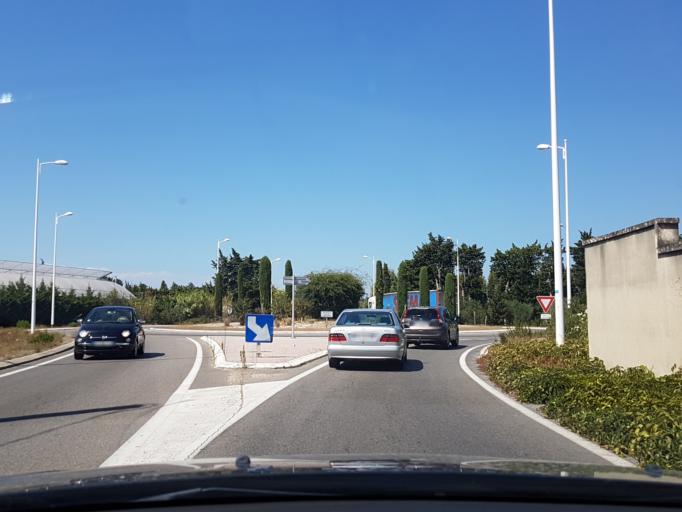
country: FR
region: Provence-Alpes-Cote d'Azur
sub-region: Departement des Bouches-du-Rhone
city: Rognonas
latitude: 43.8902
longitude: 4.8247
